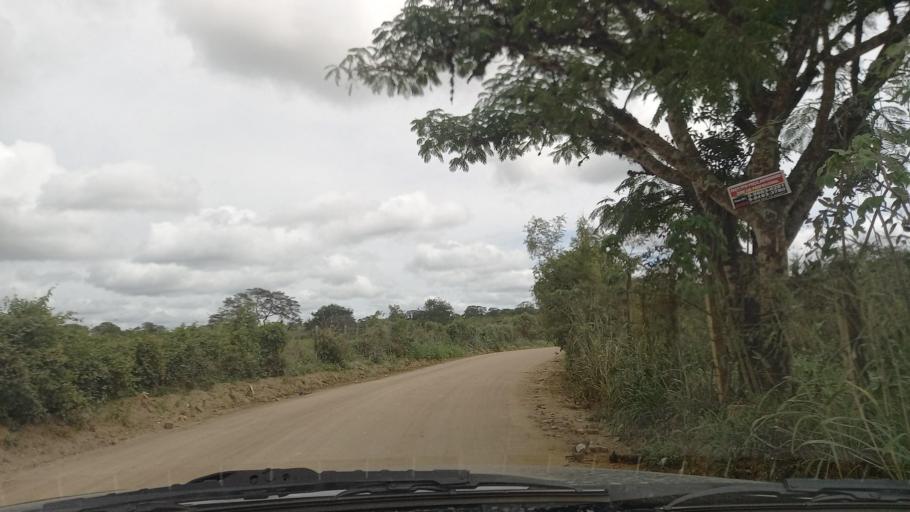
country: BR
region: Pernambuco
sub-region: Gravata
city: Gravata
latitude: -8.1838
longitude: -35.5866
